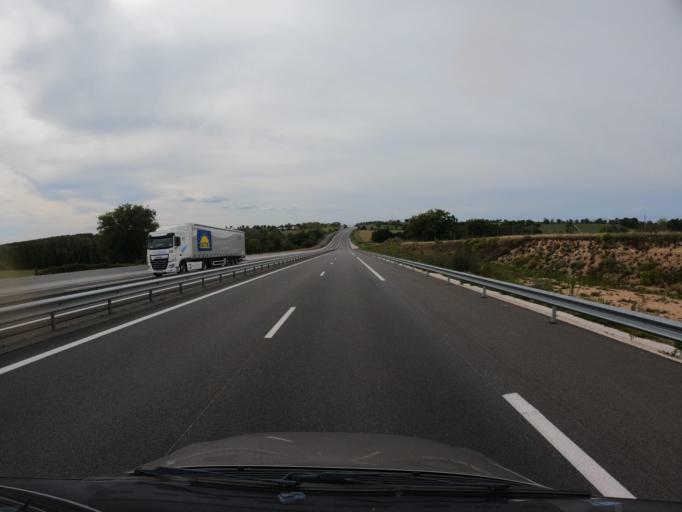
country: FR
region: Auvergne
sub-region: Departement de l'Allier
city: Montmarault
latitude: 46.3571
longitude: 3.0051
